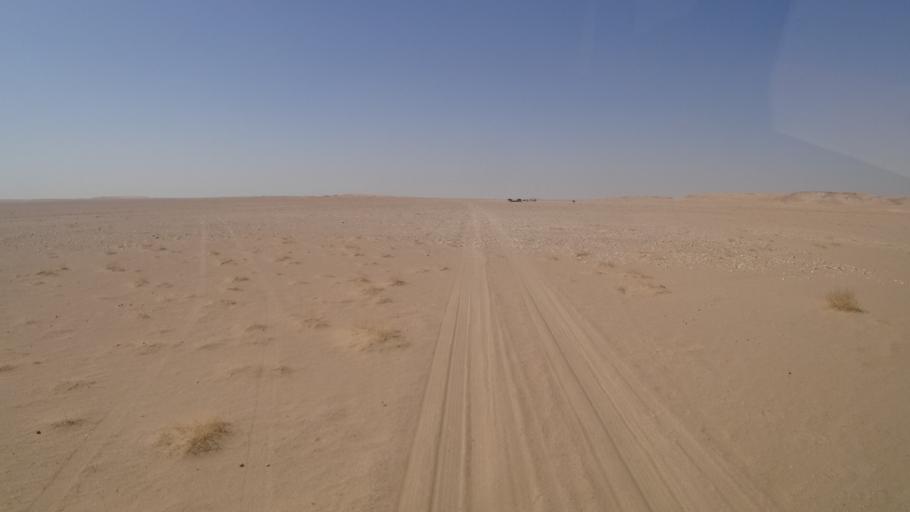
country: YE
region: Al Mahrah
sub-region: Shahan
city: Shihan as Sufla
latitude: 18.5758
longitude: 52.5001
